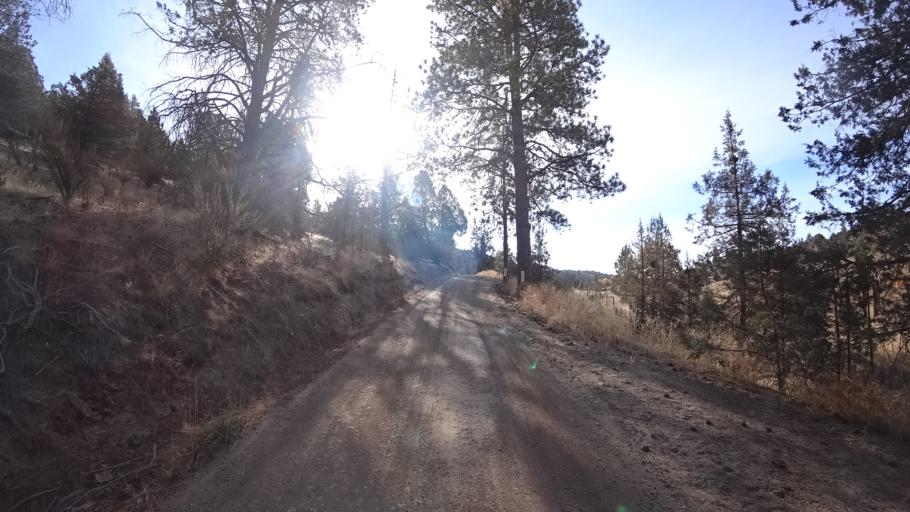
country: US
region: California
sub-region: Siskiyou County
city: Montague
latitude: 41.5963
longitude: -122.5761
